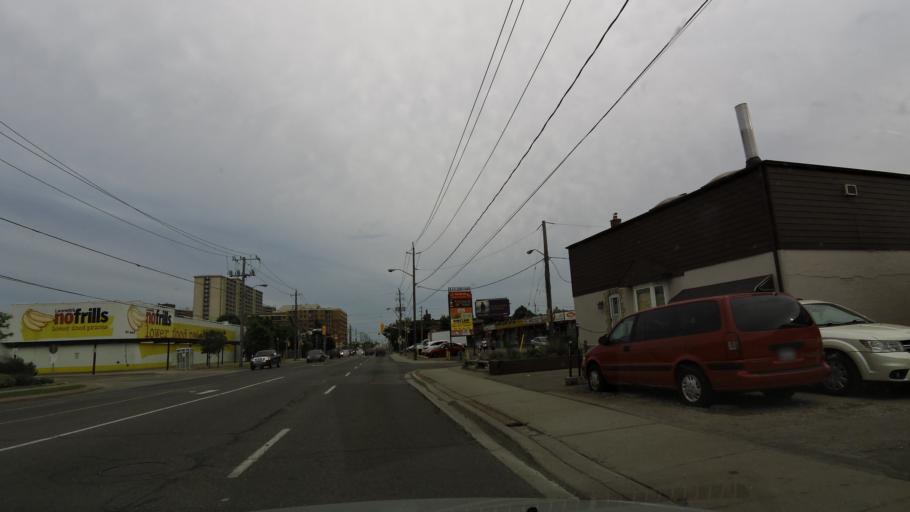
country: CA
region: Ontario
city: Etobicoke
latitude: 43.7019
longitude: -79.5036
